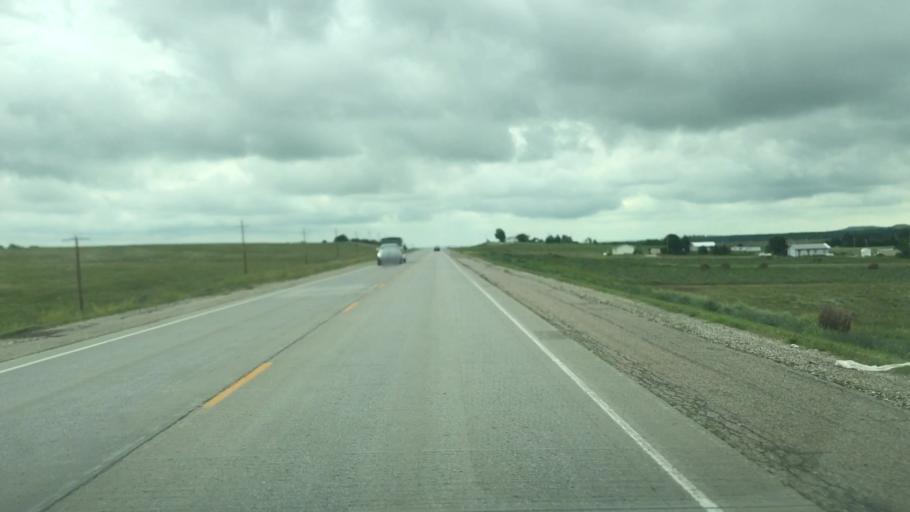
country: US
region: South Dakota
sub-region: Todd County
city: Mission
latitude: 43.3029
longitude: -100.7023
